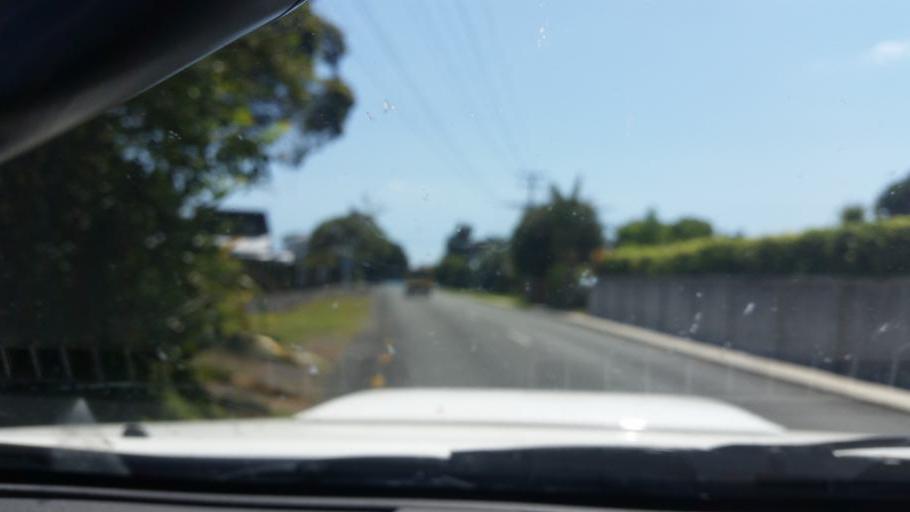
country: NZ
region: Auckland
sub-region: Auckland
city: Wellsford
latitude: -36.1248
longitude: 174.5789
